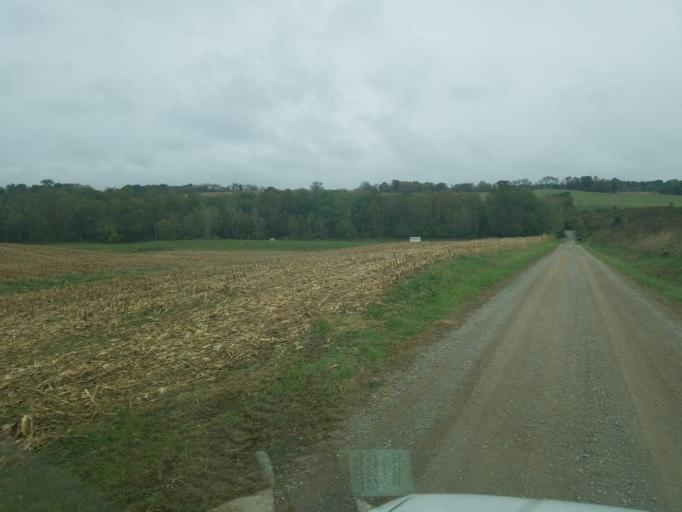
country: US
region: Ohio
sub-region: Wayne County
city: Shreve
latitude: 40.6023
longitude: -82.0480
